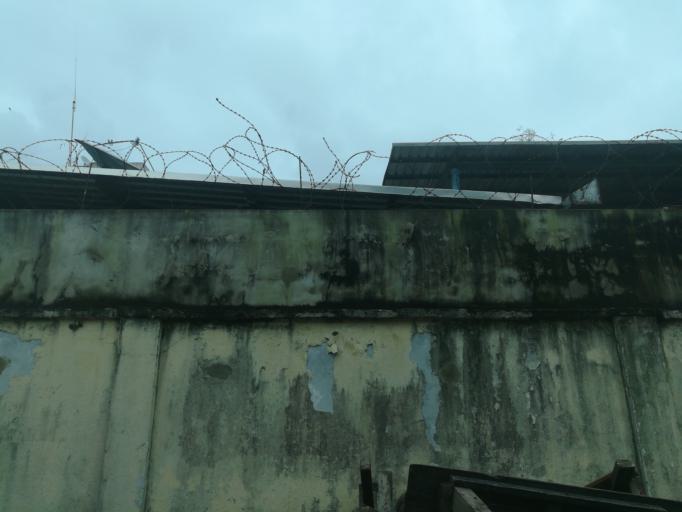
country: NG
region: Lagos
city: Ikoyi
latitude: 6.4354
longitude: 3.4207
